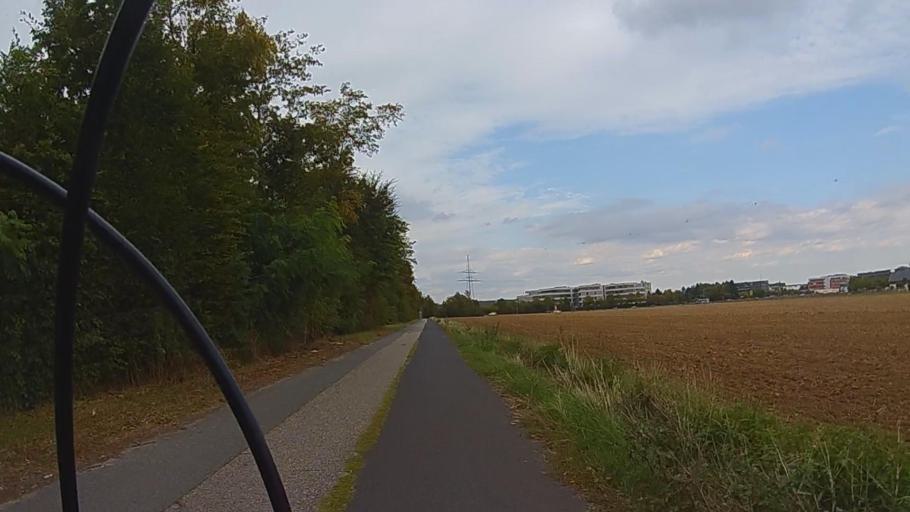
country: DE
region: Hesse
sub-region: Regierungsbezirk Darmstadt
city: Bad Homburg vor der Hoehe
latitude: 50.2088
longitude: 8.6076
